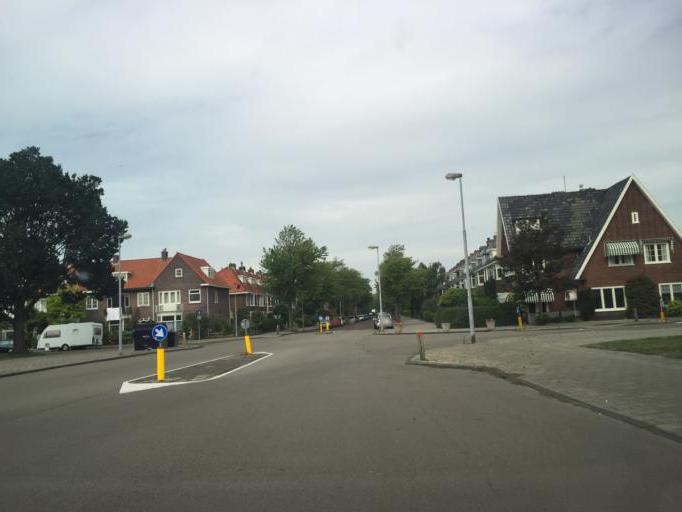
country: NL
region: North Holland
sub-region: Gemeente Bloemendaal
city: Bloemendaal
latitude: 52.4022
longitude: 4.6384
